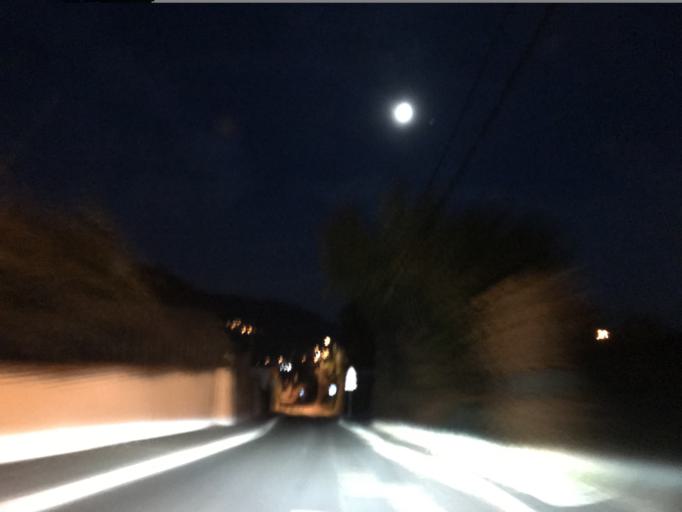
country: FR
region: Auvergne
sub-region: Departement du Puy-de-Dome
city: Thiers
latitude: 45.8590
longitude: 3.5333
